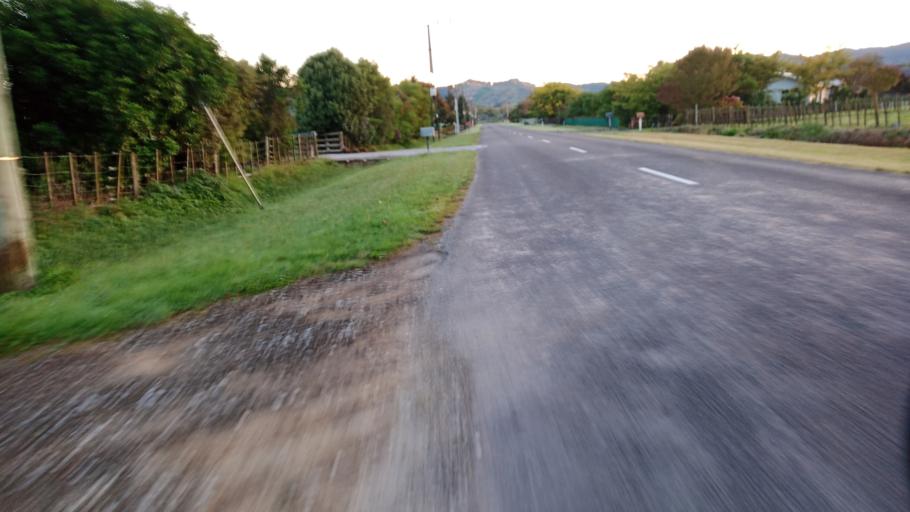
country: NZ
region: Gisborne
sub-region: Gisborne District
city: Gisborne
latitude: -38.6369
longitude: 177.9852
